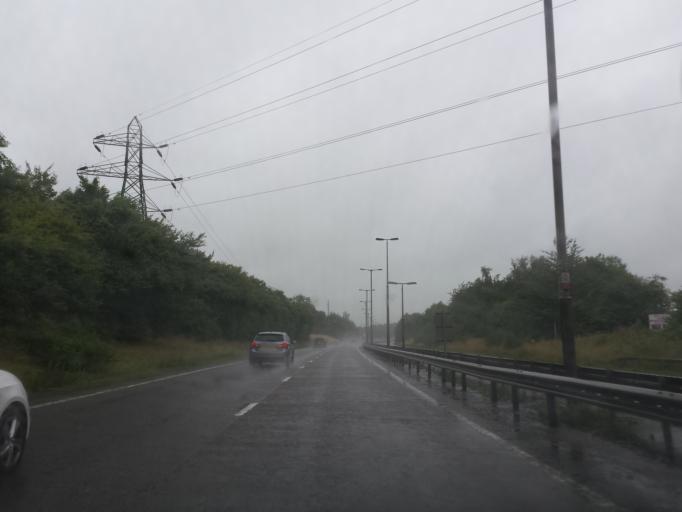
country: GB
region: England
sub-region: Warwickshire
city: Ryton on Dunsmore
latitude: 52.3935
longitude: -1.4338
